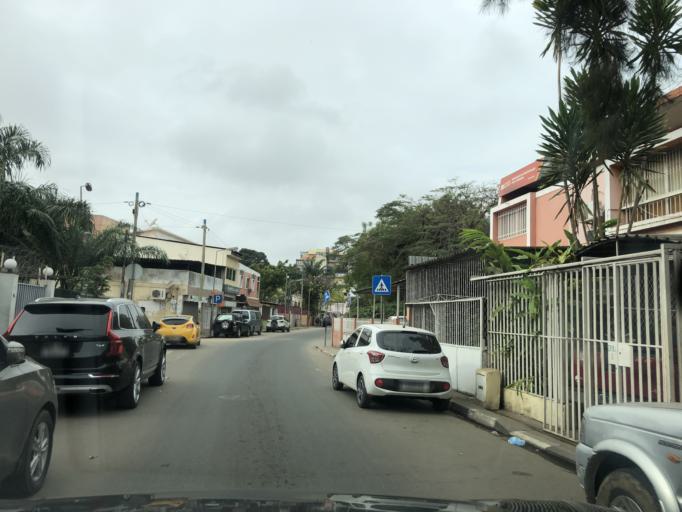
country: AO
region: Luanda
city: Luanda
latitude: -8.8195
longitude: 13.2506
